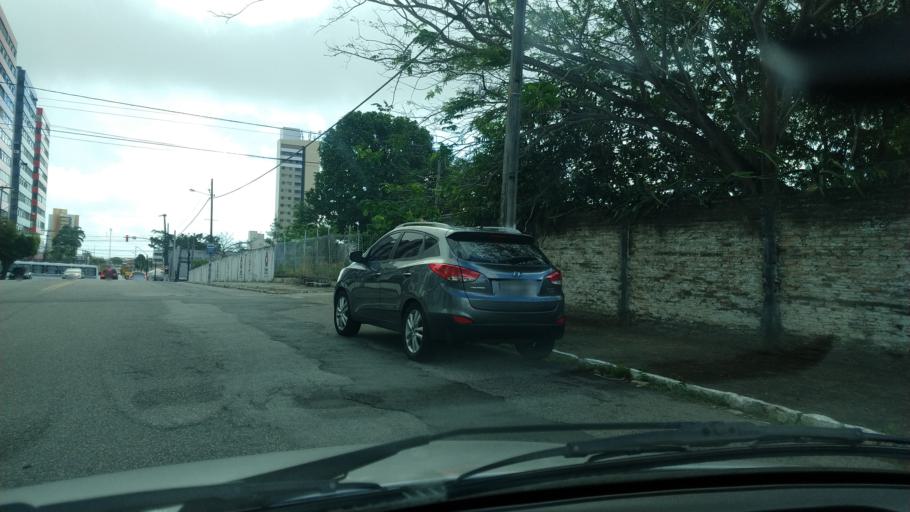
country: BR
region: Rio Grande do Norte
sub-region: Natal
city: Natal
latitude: -5.8144
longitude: -35.2199
